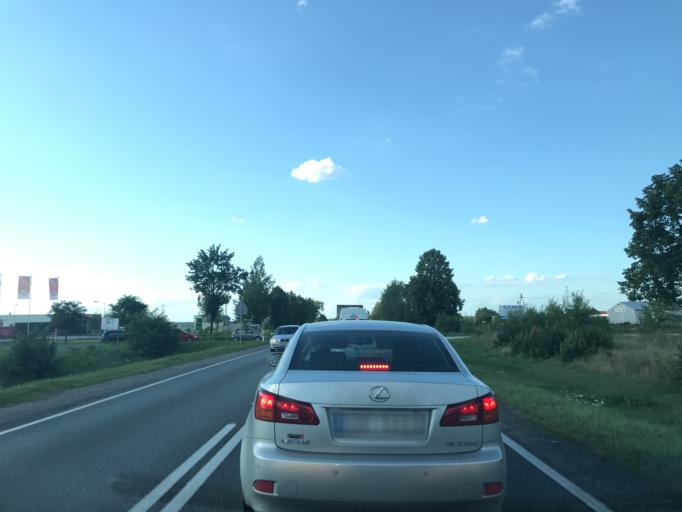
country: PL
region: Kujawsko-Pomorskie
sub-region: Powiat bydgoski
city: Biale Blota
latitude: 53.1342
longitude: 17.8797
